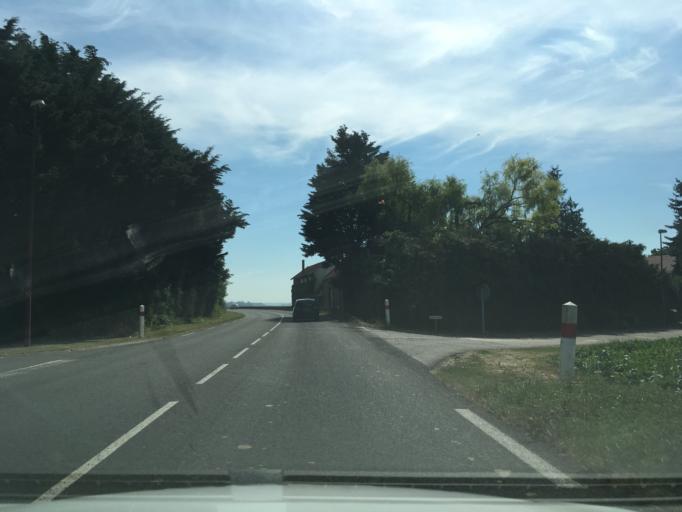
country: FR
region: Picardie
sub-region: Departement de la Somme
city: Montdidier
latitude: 49.6455
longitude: 2.6181
